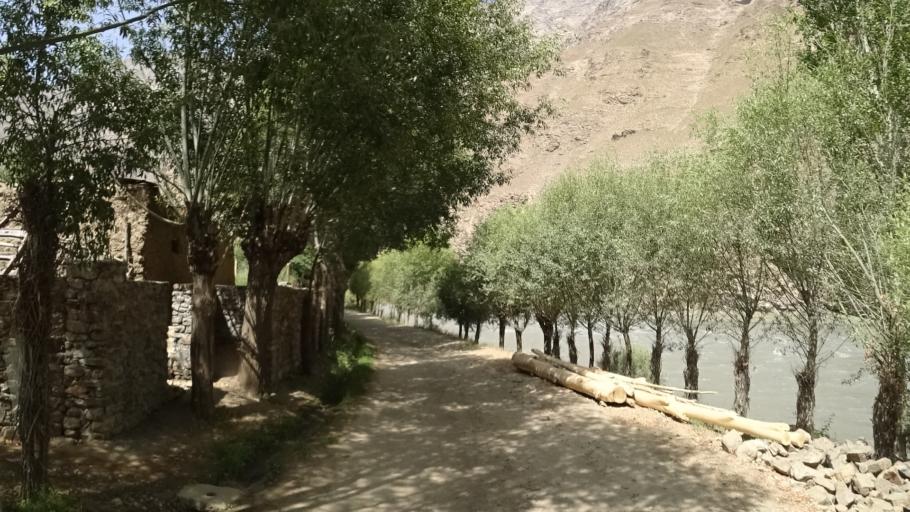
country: TJ
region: Gorno-Badakhshan
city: Khorugh
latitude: 37.1818
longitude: 71.4531
